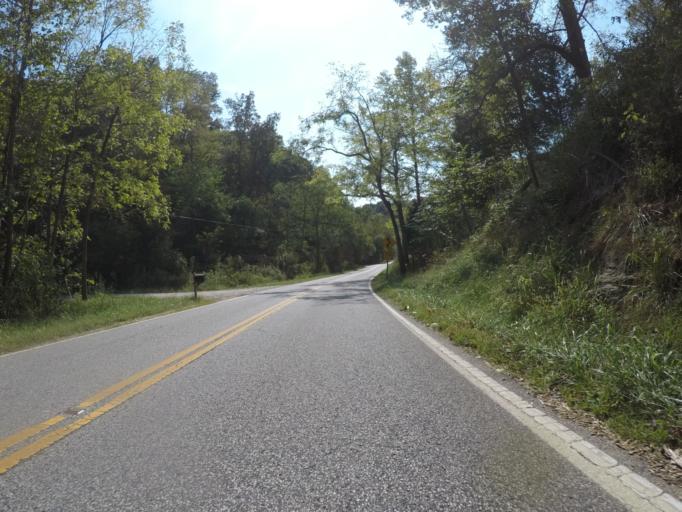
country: US
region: West Virginia
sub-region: Cabell County
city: Lesage
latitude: 38.5820
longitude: -82.4188
